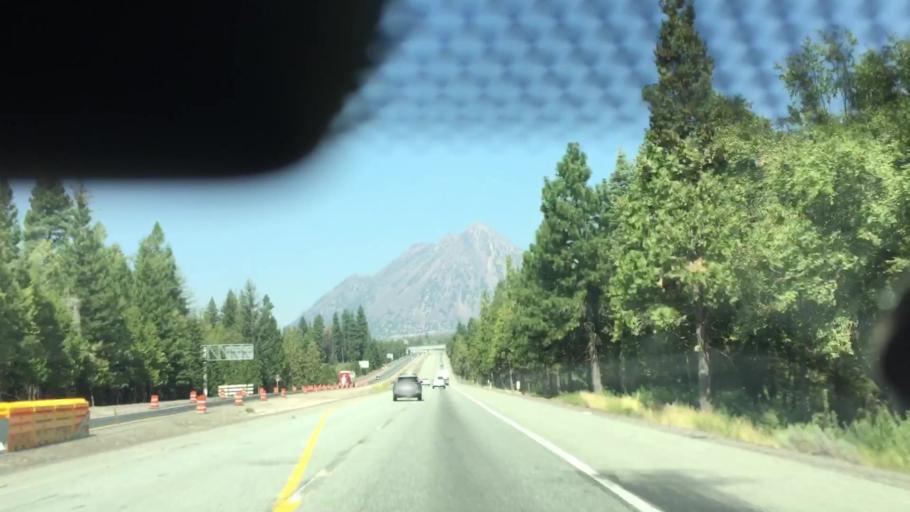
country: US
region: California
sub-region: Siskiyou County
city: Mount Shasta
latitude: 41.3226
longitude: -122.3268
